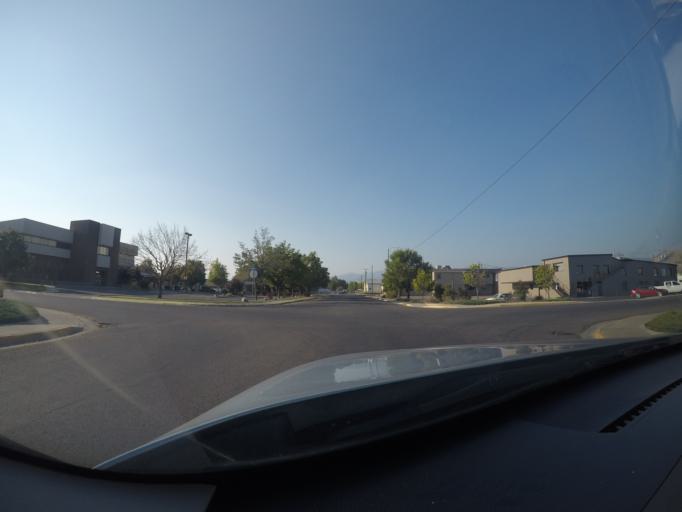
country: US
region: Montana
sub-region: Missoula County
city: Missoula
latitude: 46.8532
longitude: -114.0165
